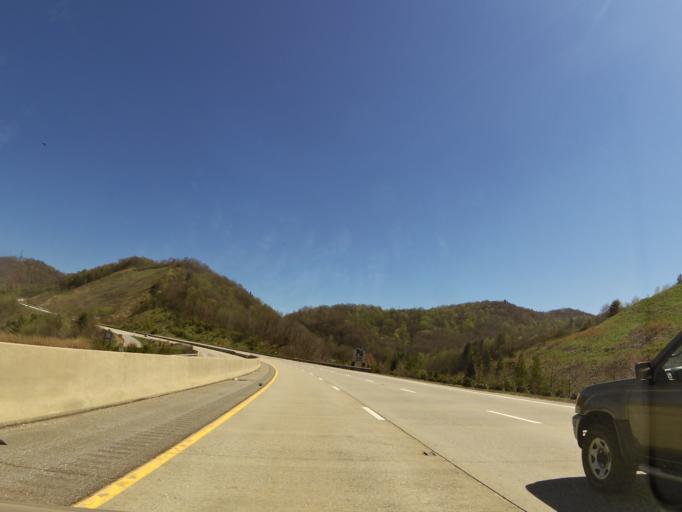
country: US
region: North Carolina
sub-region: Madison County
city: Mars Hill
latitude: 35.9106
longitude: -82.5586
